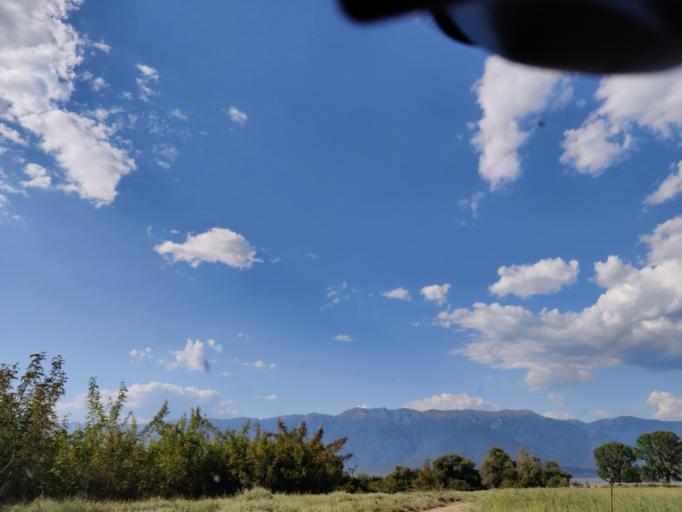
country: GR
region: Central Macedonia
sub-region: Nomos Serron
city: Chrysochorafa
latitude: 41.1849
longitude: 23.1078
